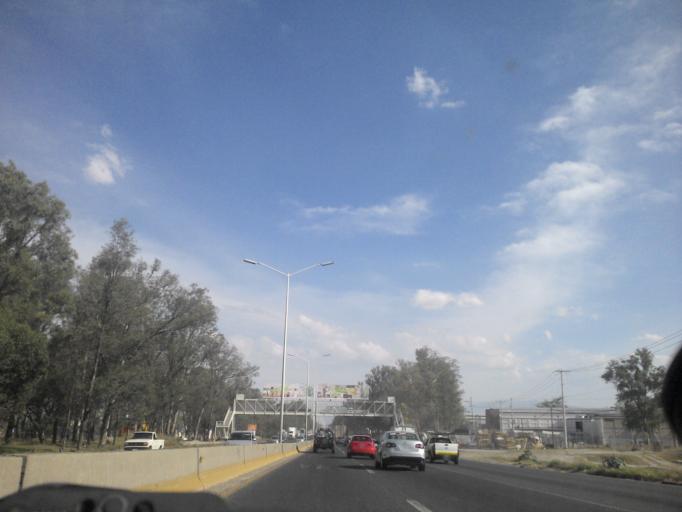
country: MX
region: Jalisco
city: Guadalajara
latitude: 20.6676
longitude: -103.4513
